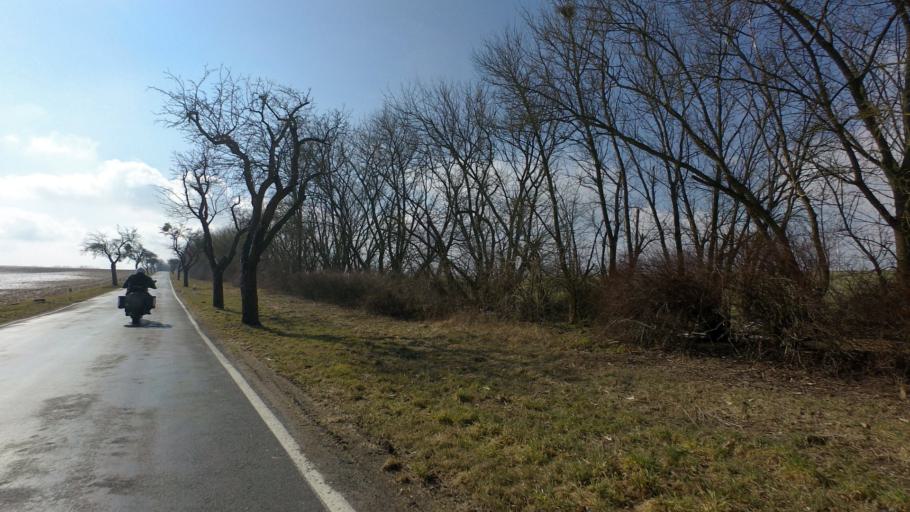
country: DE
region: Brandenburg
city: Melchow
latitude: 52.7043
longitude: 13.7193
